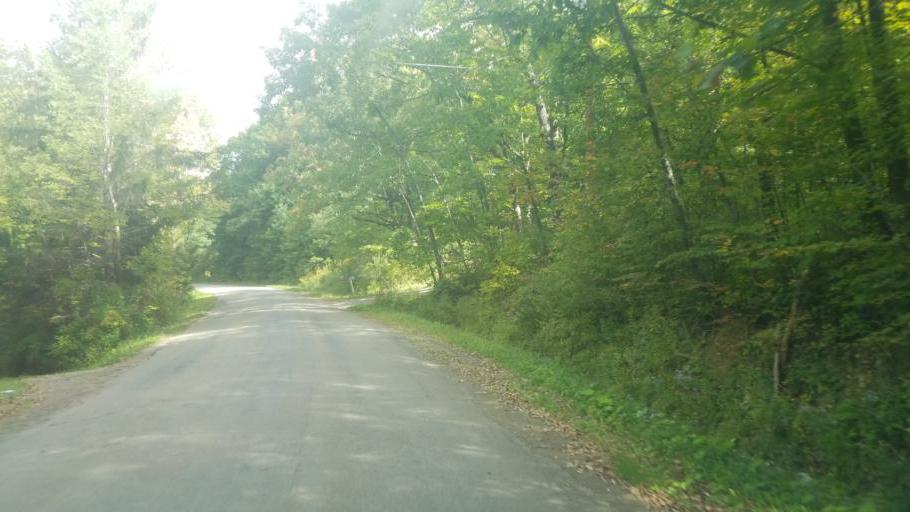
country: US
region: New York
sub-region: Cattaraugus County
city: Weston Mills
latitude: 42.1591
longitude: -78.3619
